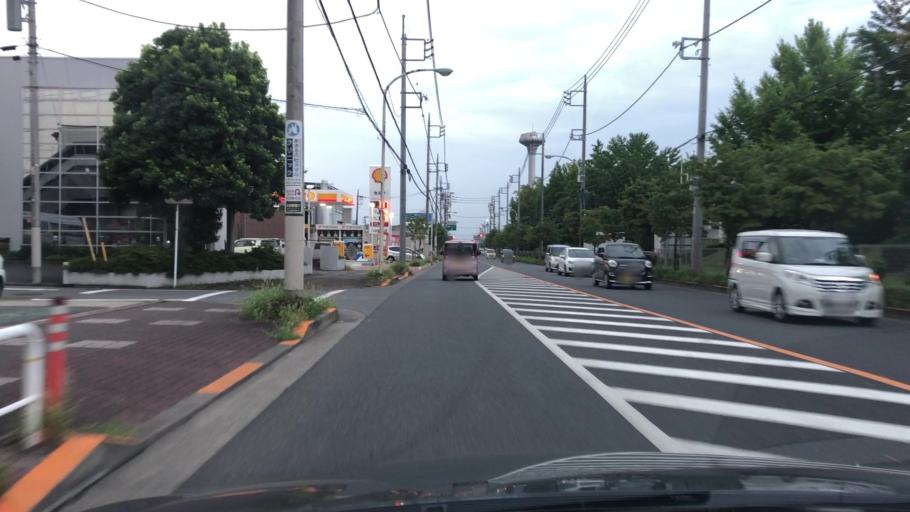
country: JP
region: Tokyo
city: Fussa
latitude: 35.7395
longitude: 139.2786
